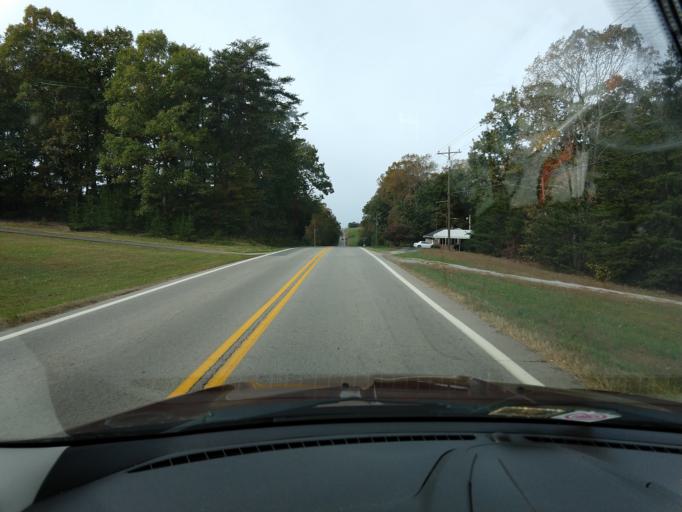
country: US
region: Virginia
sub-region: Pittsylvania County
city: Gretna
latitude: 36.9542
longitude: -79.4082
